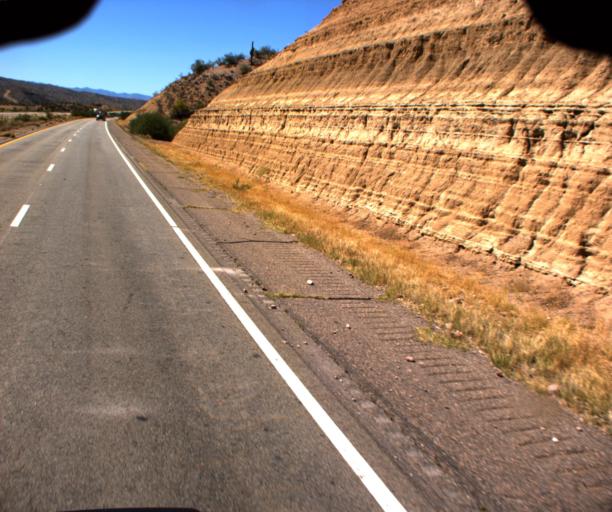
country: US
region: Arizona
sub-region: Yavapai County
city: Bagdad
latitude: 34.6411
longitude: -113.5631
